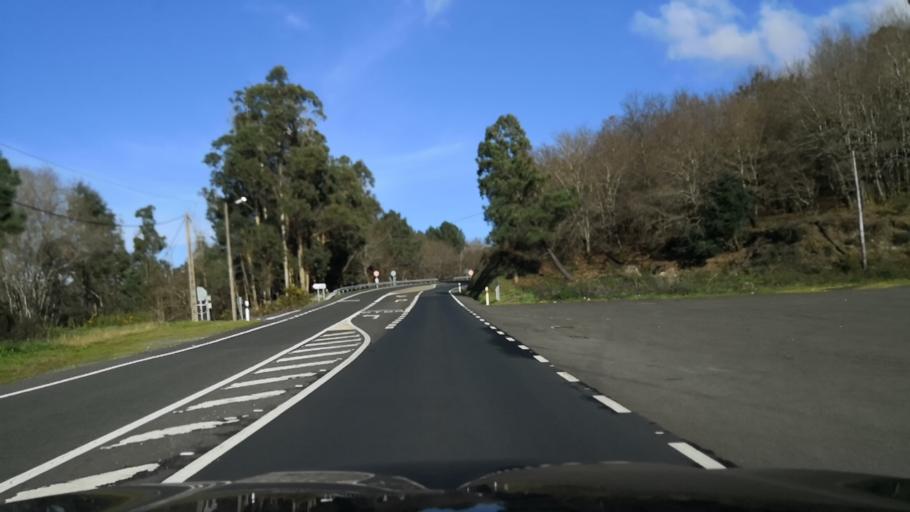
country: ES
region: Galicia
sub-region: Provincia da Coruna
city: Ribeira
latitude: 42.7074
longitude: -8.3950
